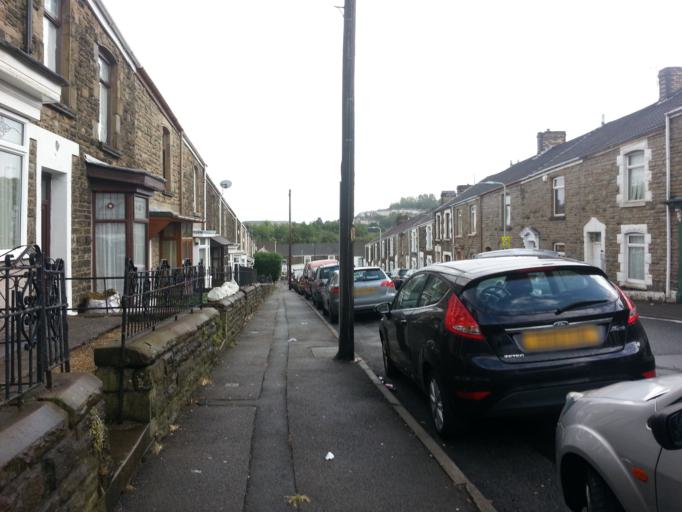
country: GB
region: Wales
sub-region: City and County of Swansea
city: Landore
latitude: 51.6372
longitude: -3.9493
